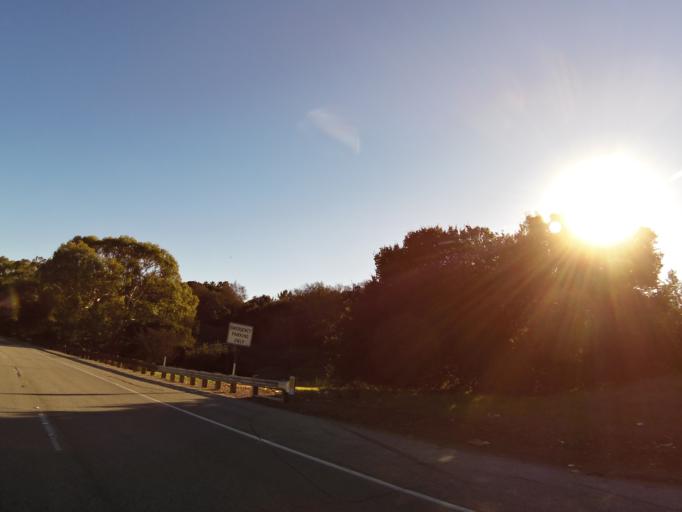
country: US
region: California
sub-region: Santa Clara County
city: Los Altos Hills
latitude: 37.3788
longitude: -122.1508
